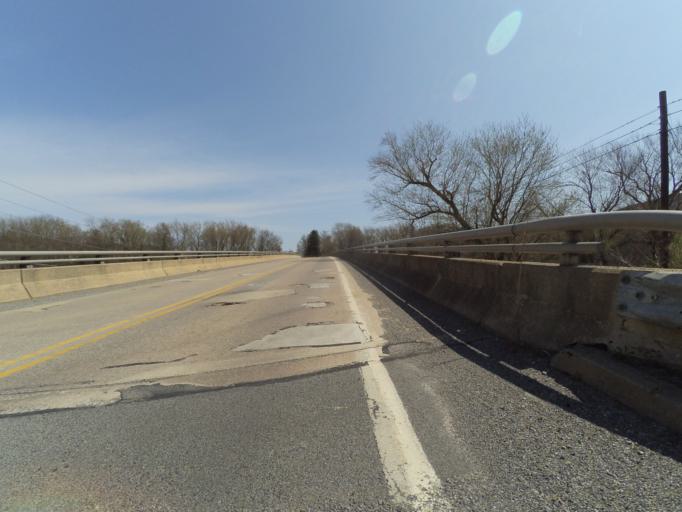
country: US
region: Pennsylvania
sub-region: Clinton County
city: Dunnstown
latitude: 41.1428
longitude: -77.3986
